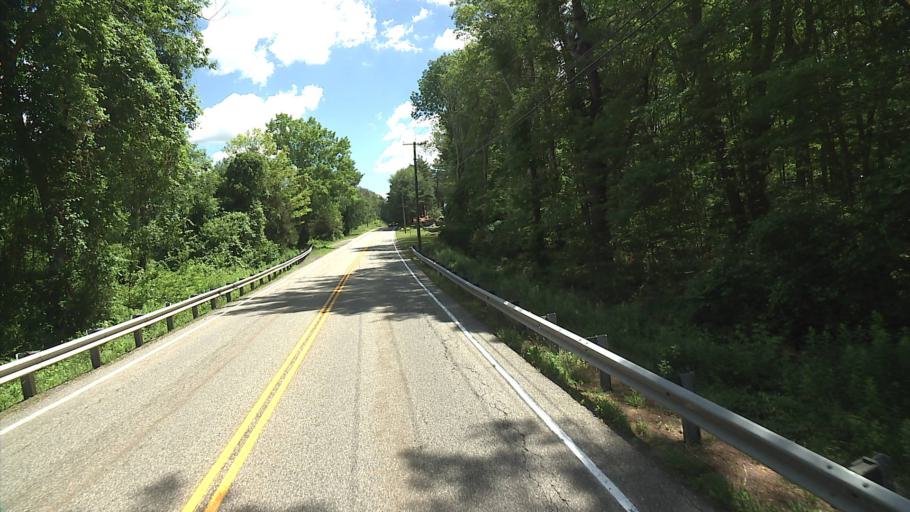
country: US
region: Connecticut
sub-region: New London County
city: Old Mystic
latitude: 41.4010
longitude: -71.9524
